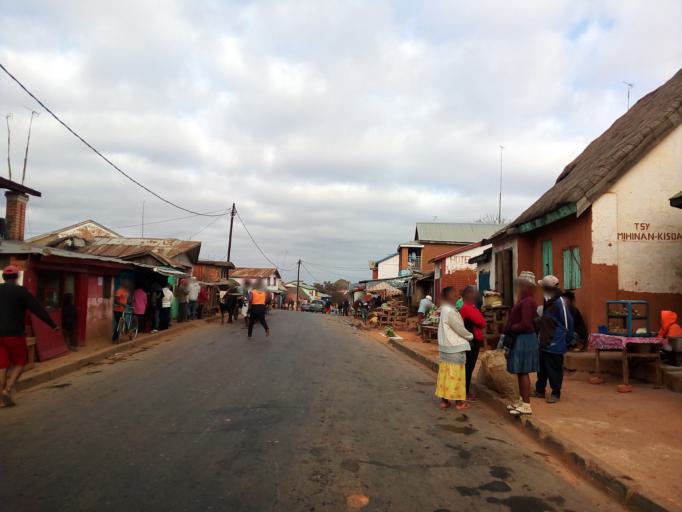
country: MG
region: Analamanga
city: Ankazobe
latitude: -18.6404
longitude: 47.2732
